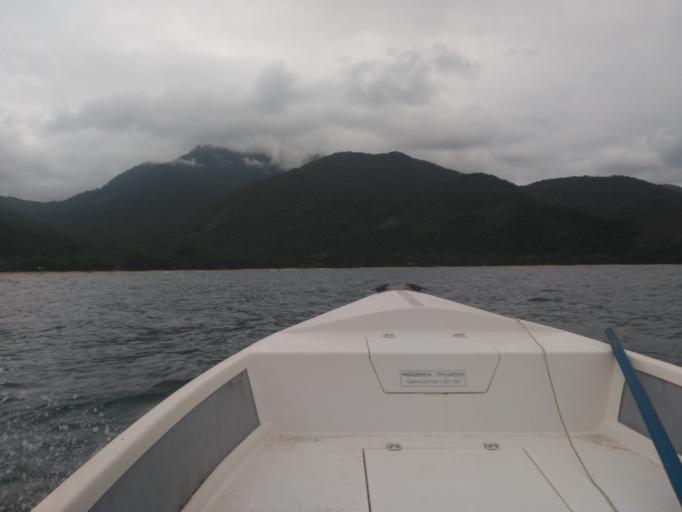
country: BR
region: Rio de Janeiro
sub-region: Parati
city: Paraty
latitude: -23.3378
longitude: -44.6379
